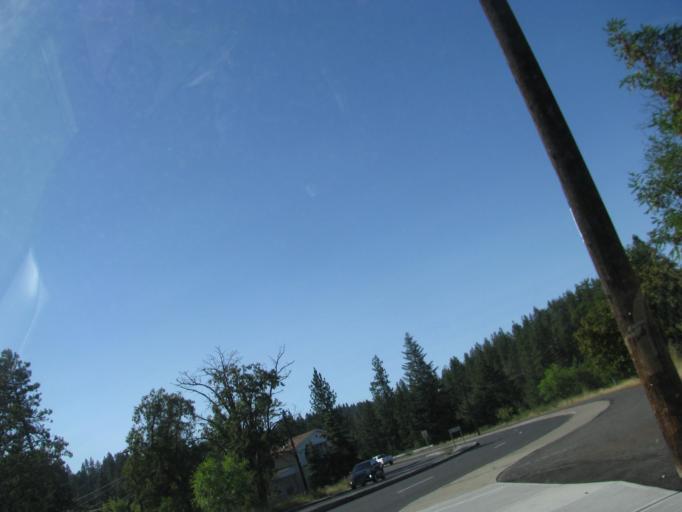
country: US
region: Washington
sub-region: Spokane County
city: Spokane
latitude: 47.6554
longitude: -117.4613
